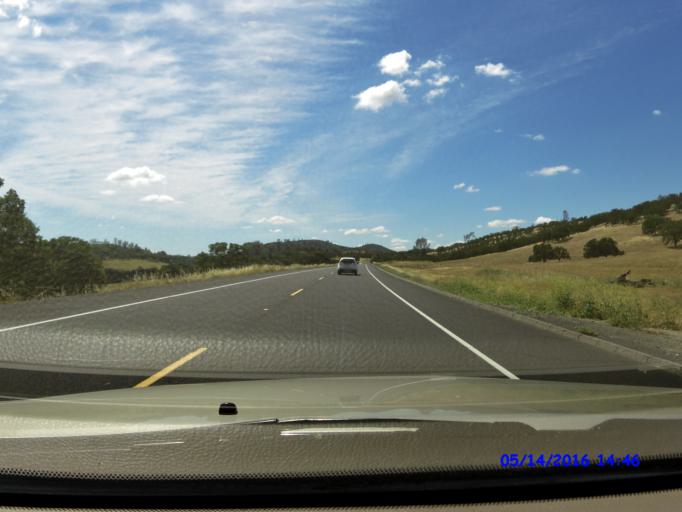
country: US
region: California
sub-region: Tuolumne County
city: Jamestown
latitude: 37.8502
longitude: -120.4016
